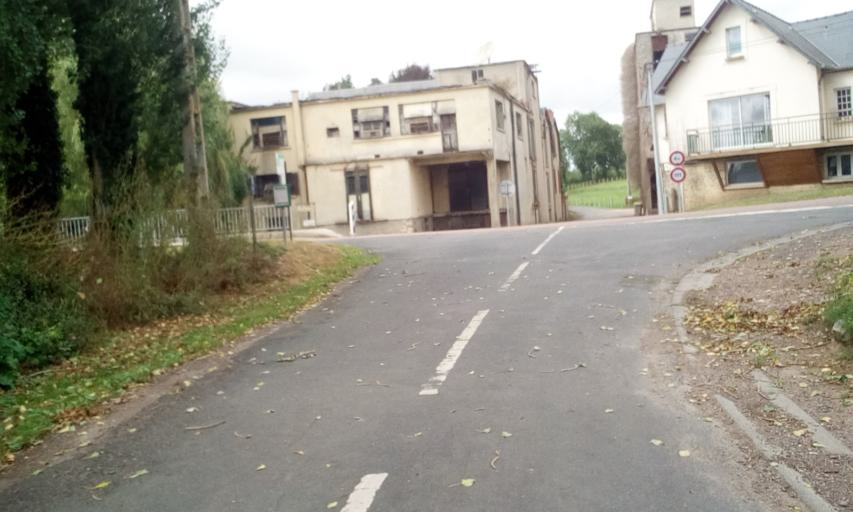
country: FR
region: Lower Normandy
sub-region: Departement du Calvados
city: Tilly-sur-Seulles
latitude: 49.2131
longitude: -0.6223
